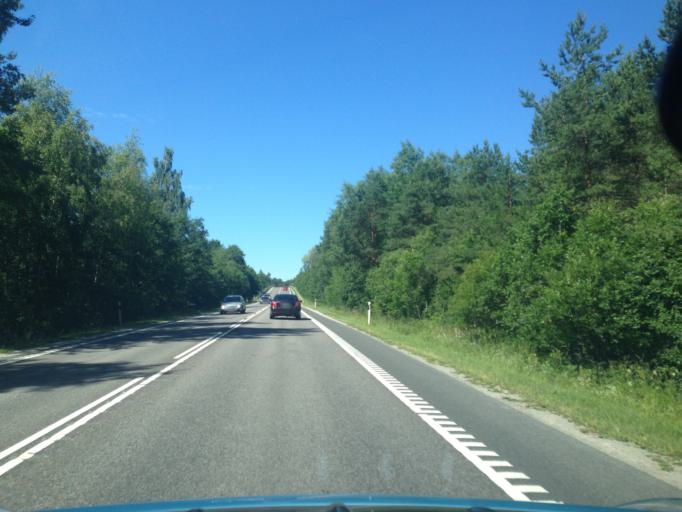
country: EE
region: Harju
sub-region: Saue linn
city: Saue
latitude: 59.3151
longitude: 24.5254
